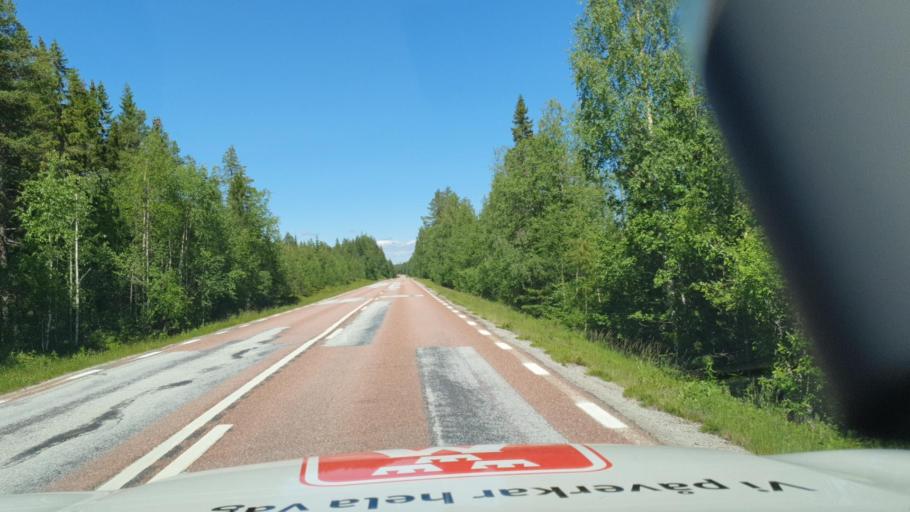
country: SE
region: Jaemtland
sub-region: Harjedalens Kommun
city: Sveg
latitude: 61.8758
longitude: 14.6289
